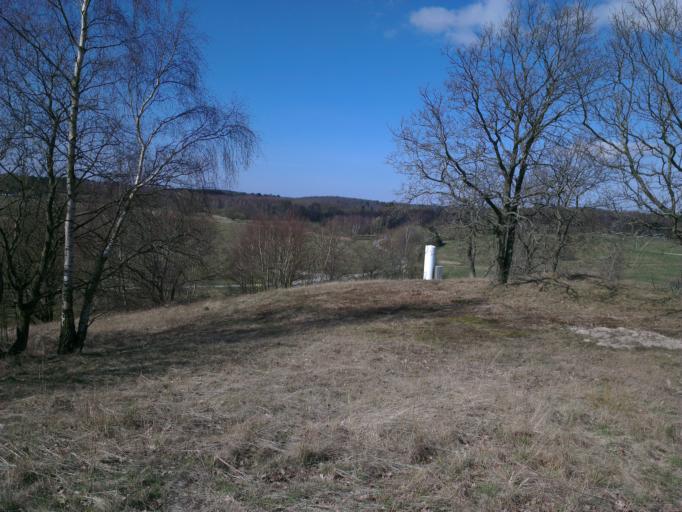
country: DK
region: Capital Region
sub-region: Frederikssund Kommune
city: Jaegerspris
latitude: 55.8914
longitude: 11.9671
